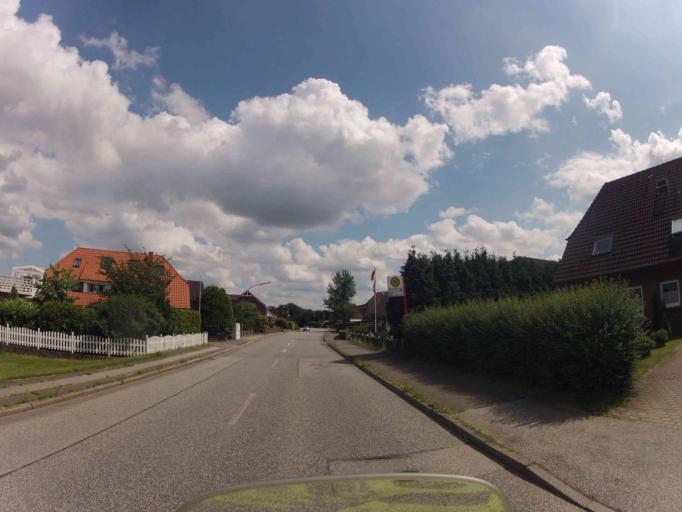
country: DE
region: Lower Saxony
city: Stelle
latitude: 53.4239
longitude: 10.1399
